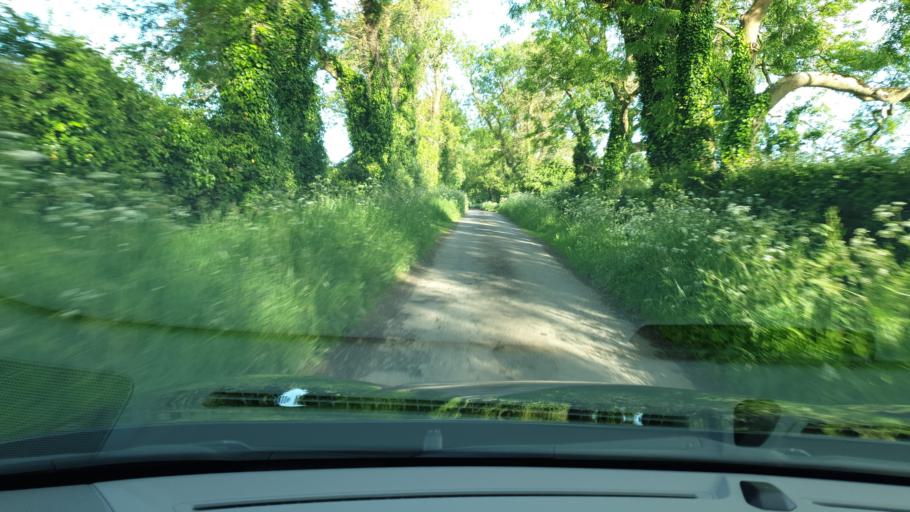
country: IE
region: Leinster
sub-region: An Mhi
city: Ashbourne
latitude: 53.5534
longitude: -6.4255
